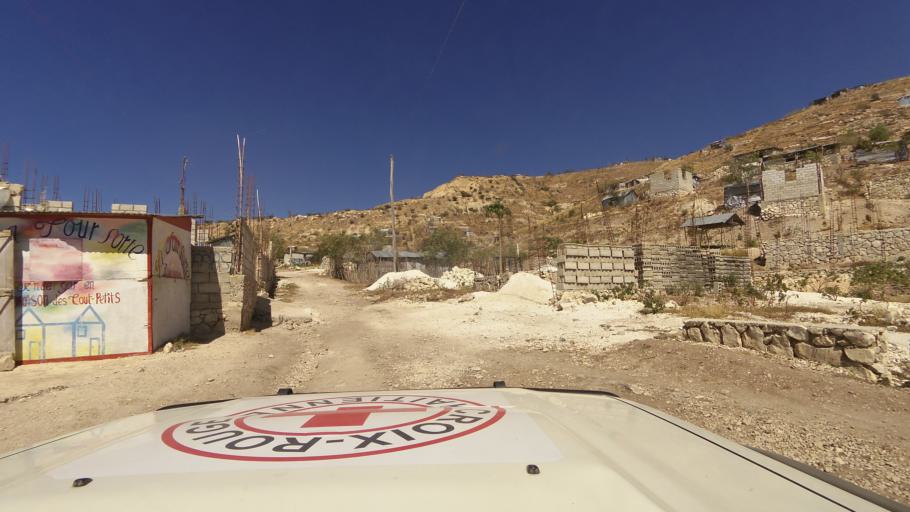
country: HT
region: Ouest
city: Croix des Bouquets
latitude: 18.6640
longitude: -72.2695
